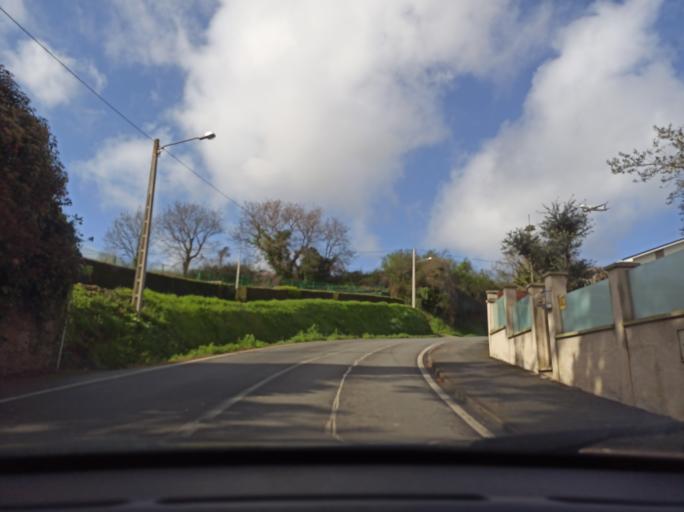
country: ES
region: Galicia
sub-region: Provincia da Coruna
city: Cambre
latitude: 43.3241
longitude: -8.3535
